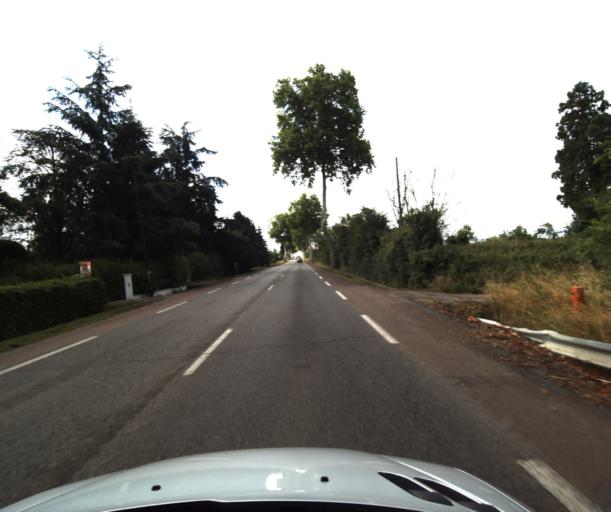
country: FR
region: Midi-Pyrenees
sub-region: Departement du Tarn-et-Garonne
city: Moissac
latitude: 44.0704
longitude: 1.0947
